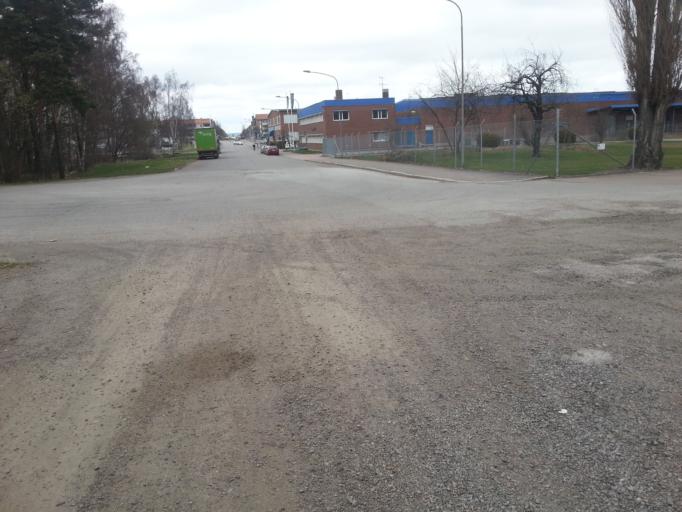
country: SE
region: OEstergoetland
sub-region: Norrkopings Kommun
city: Norrkoping
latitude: 58.5938
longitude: 16.1539
